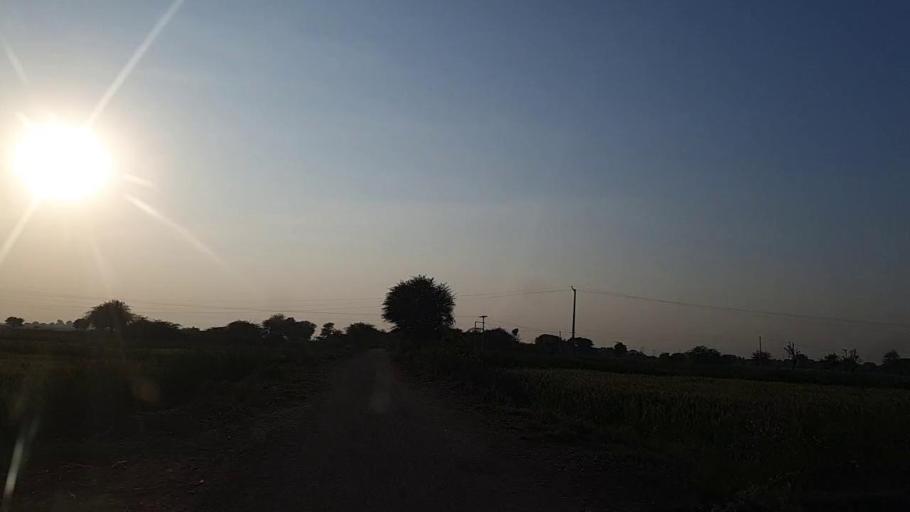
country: PK
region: Sindh
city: Naukot
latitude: 24.9587
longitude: 69.4512
